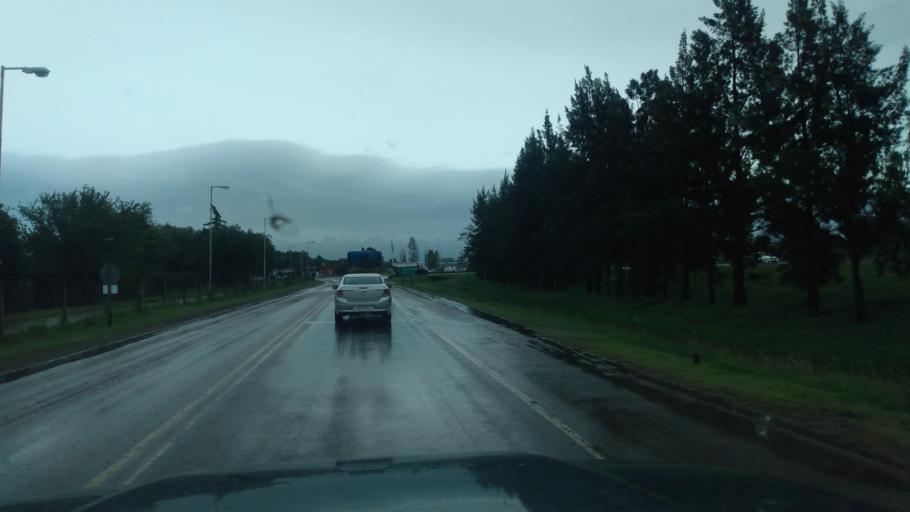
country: AR
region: Buenos Aires
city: Capilla del Senor
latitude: -34.3918
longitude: -59.0369
